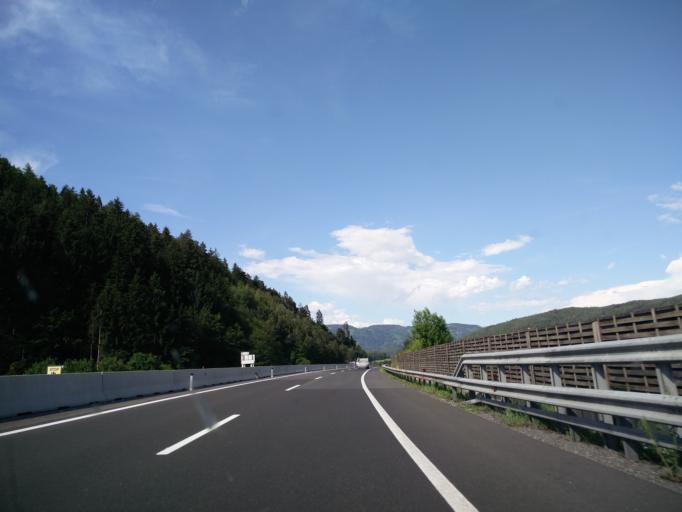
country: AT
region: Carinthia
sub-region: Politischer Bezirk Volkermarkt
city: Voelkermarkt
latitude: 46.6541
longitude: 14.5641
